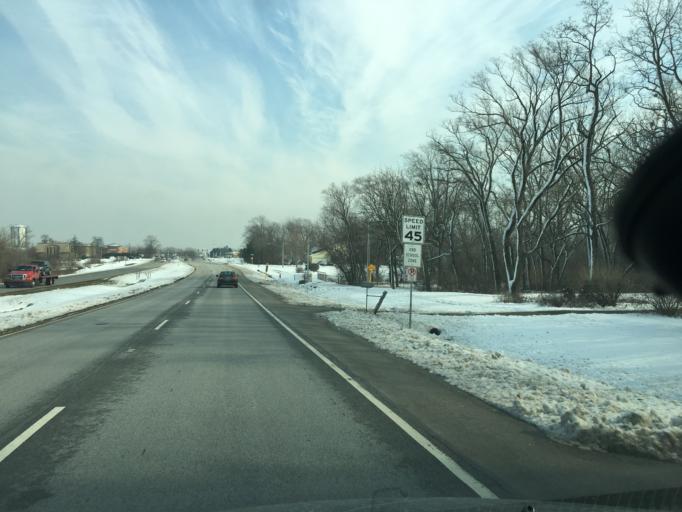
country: US
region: Illinois
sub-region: DuPage County
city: Willowbrook
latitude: 41.7522
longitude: -87.9507
